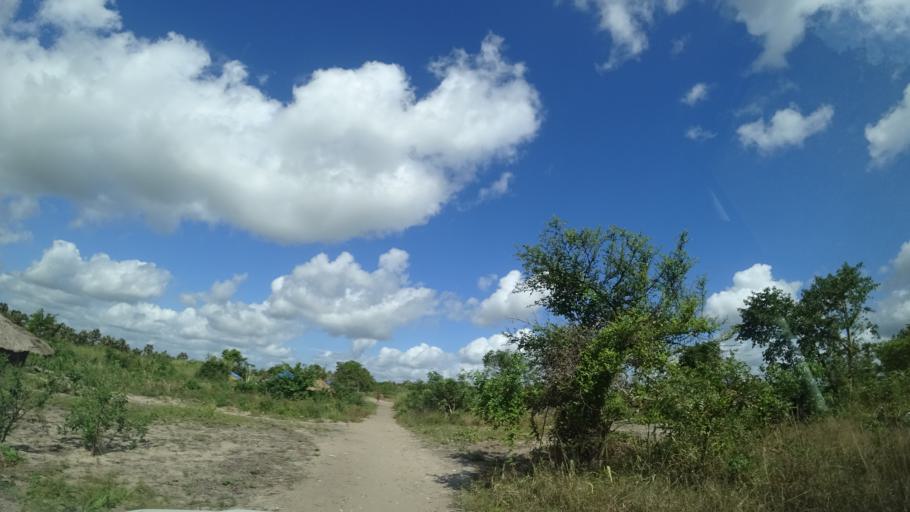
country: MZ
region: Sofala
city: Dondo
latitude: -19.3574
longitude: 34.5794
